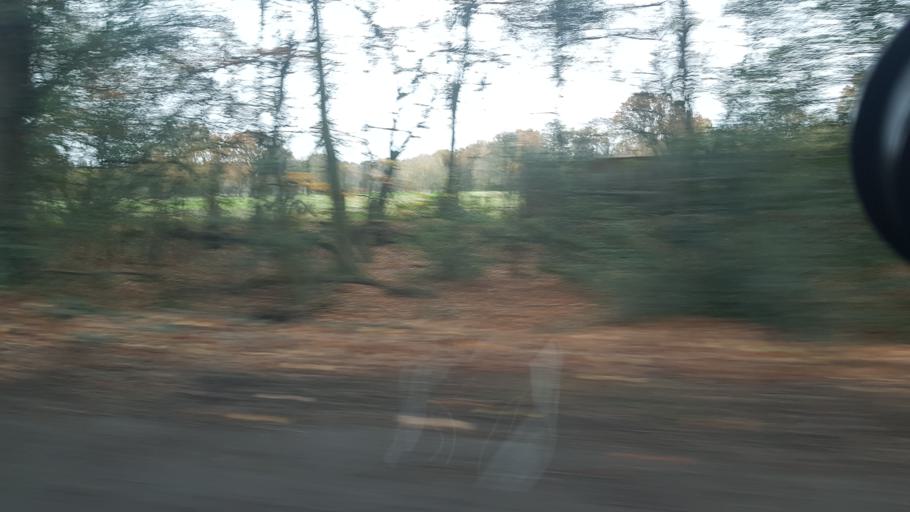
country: GB
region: England
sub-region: Hampshire
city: Eversley
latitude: 51.3513
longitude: -0.8874
